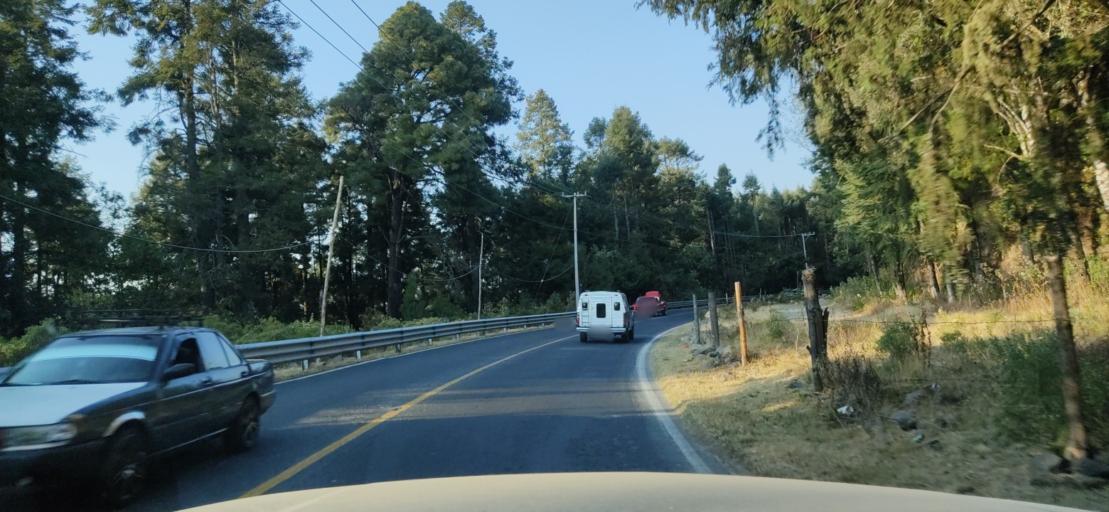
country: MX
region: Mexico
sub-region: Ocoyoacac
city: San Jeronimo Acazulco
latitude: 19.2579
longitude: -99.3784
